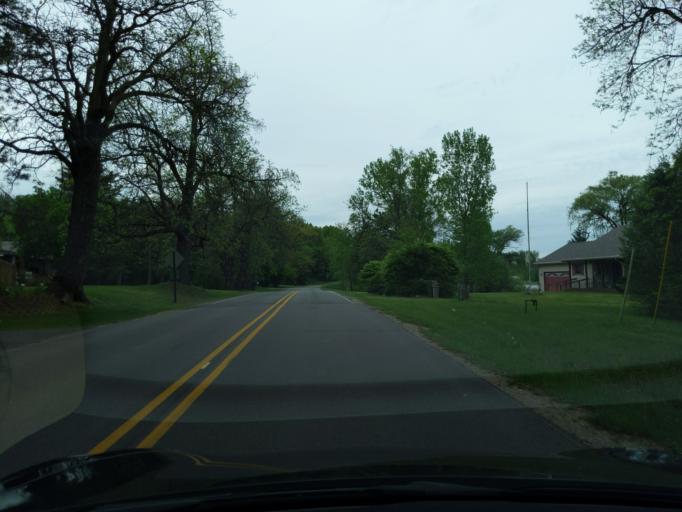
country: US
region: Michigan
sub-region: Jackson County
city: Jackson
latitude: 42.3571
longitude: -84.3498
